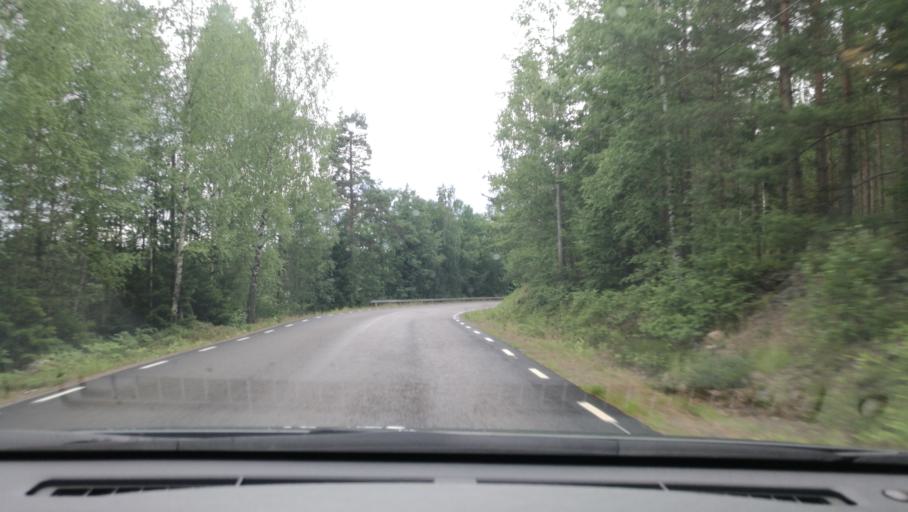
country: SE
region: OEstergoetland
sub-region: Norrkopings Kommun
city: Jursla
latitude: 58.8069
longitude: 16.1035
